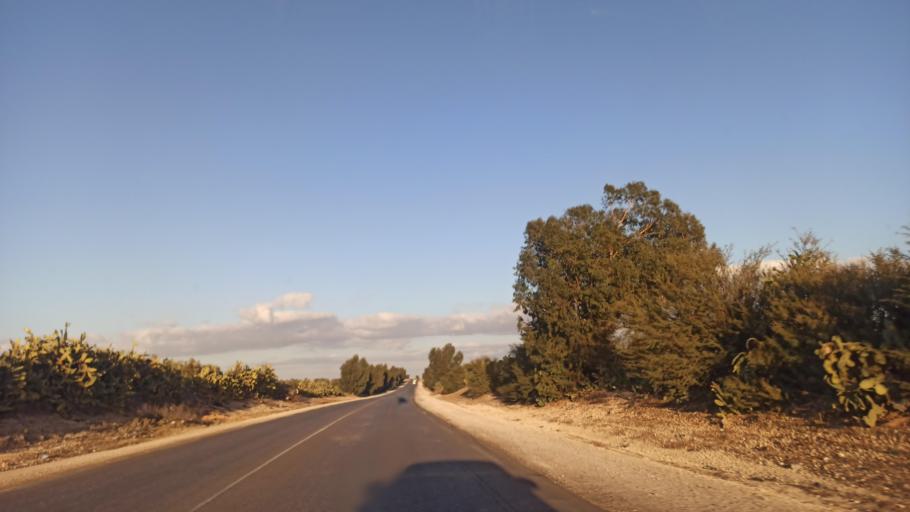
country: TN
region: Al Qayrawan
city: Sbikha
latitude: 35.8447
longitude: 10.1850
